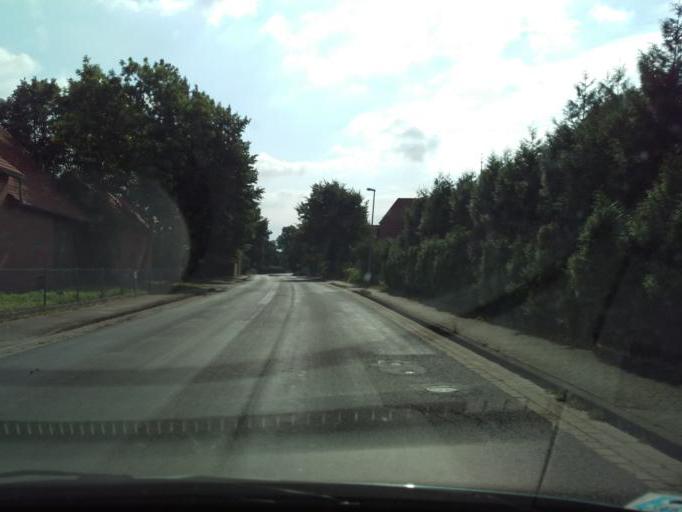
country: DE
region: Lower Saxony
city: Arpke
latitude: 52.3751
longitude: 10.1332
